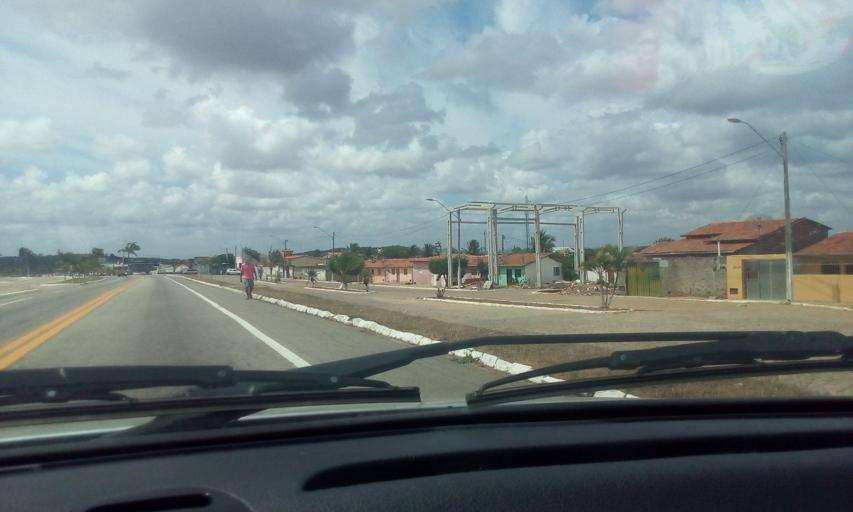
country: BR
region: Rio Grande do Norte
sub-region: Tangara
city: Tangara
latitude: -6.1049
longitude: -35.7067
